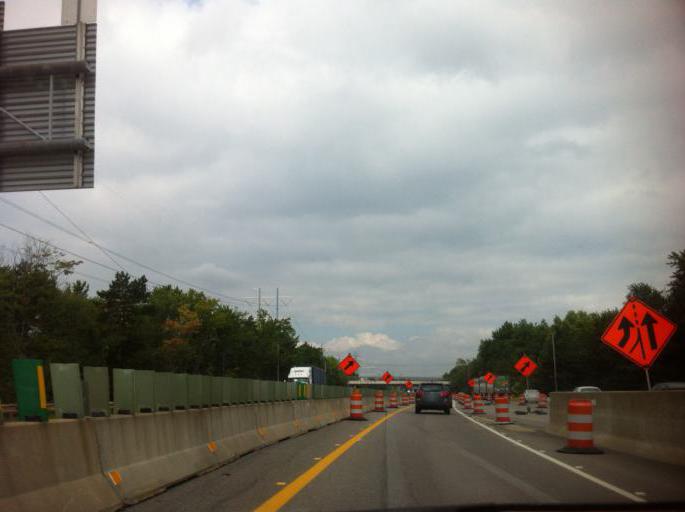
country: US
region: Ohio
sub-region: Cuyahoga County
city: Berea
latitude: 41.3455
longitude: -81.8534
